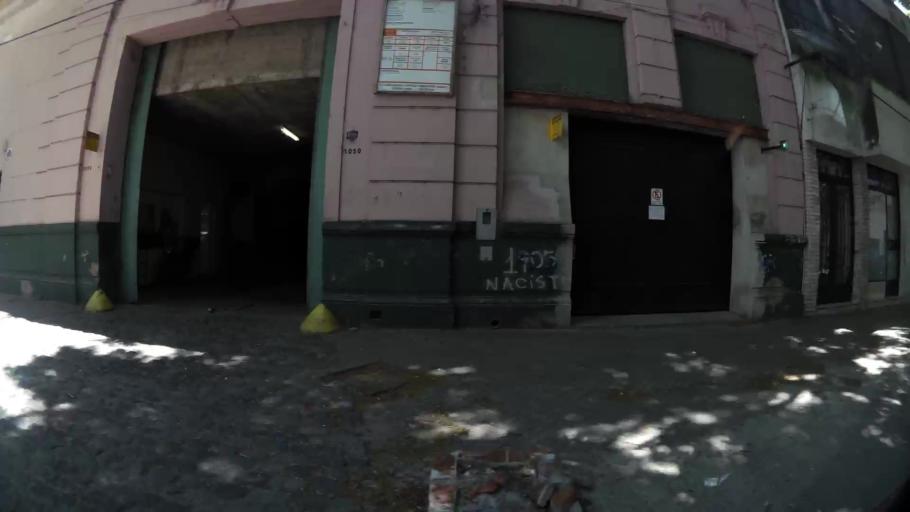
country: AR
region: Santa Fe
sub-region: Departamento de Rosario
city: Rosario
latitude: -32.9457
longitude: -60.6610
